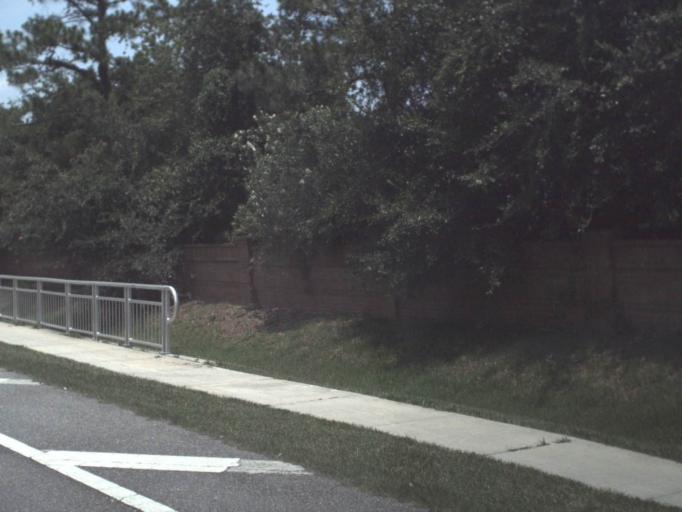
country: US
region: Florida
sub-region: Saint Johns County
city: Ponte Vedra Beach
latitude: 30.2211
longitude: -81.3830
